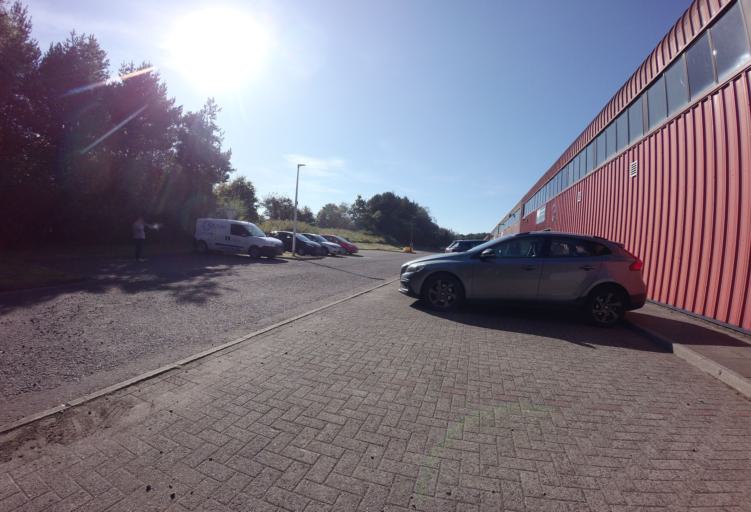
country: GB
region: Scotland
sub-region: West Lothian
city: West Calder
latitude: 55.8962
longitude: -3.5726
